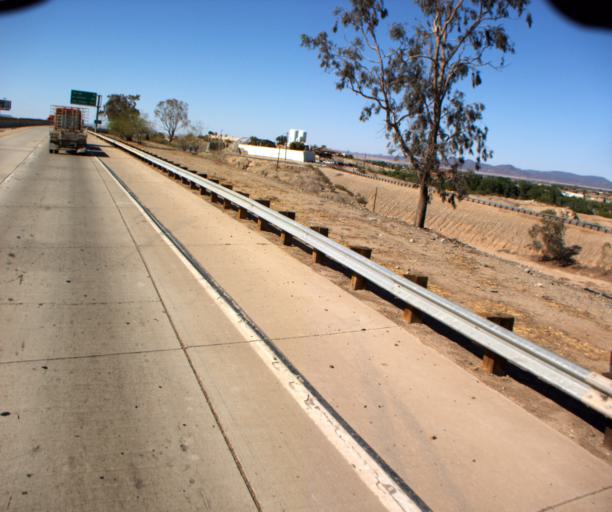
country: US
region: Arizona
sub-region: Yuma County
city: Yuma
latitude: 32.7234
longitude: -114.6140
